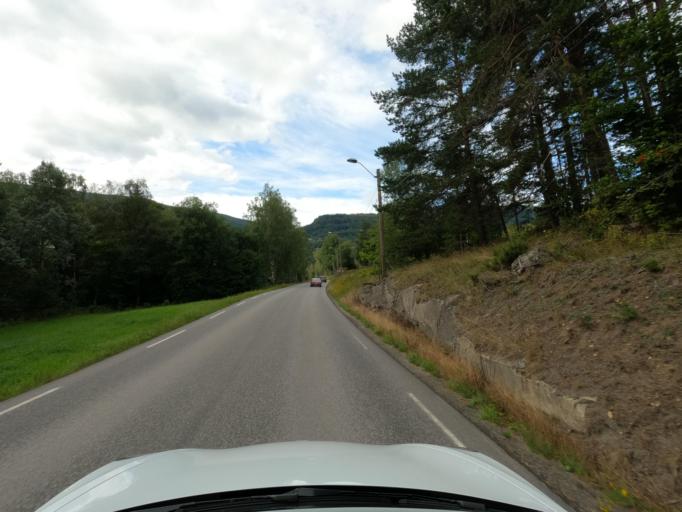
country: NO
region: Telemark
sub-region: Tinn
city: Rjukan
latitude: 59.9896
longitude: 8.7390
